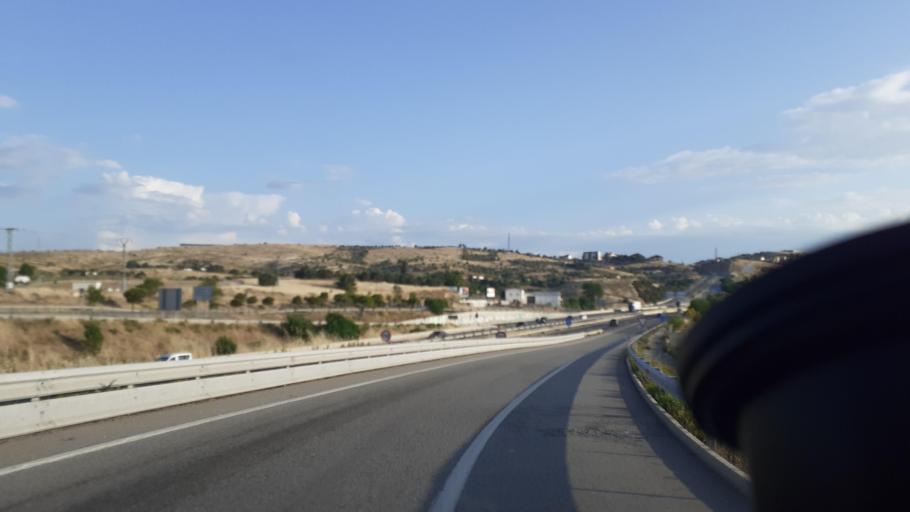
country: ES
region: Madrid
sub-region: Provincia de Madrid
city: El Molar
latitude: 40.7170
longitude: -3.5765
